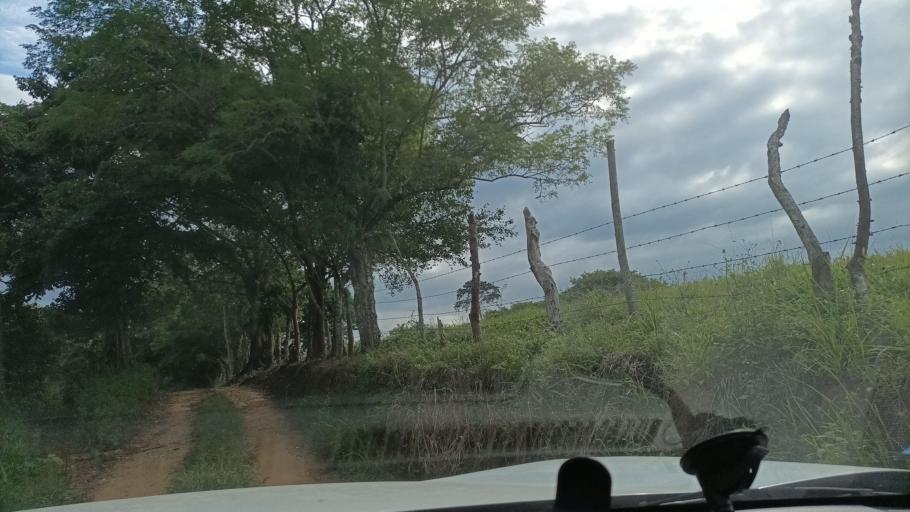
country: MX
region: Veracruz
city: Soconusco
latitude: 17.9464
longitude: -94.8828
